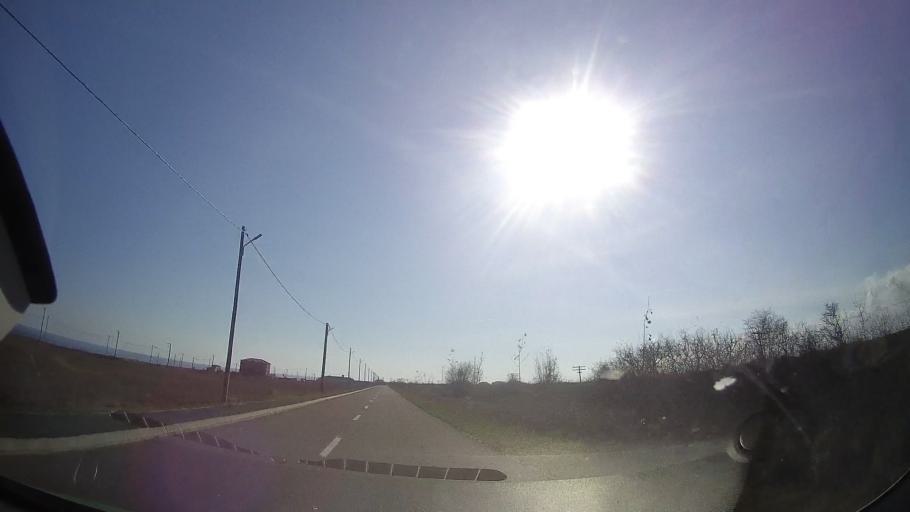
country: RO
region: Constanta
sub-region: Comuna Costinesti
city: Schitu
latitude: 43.9307
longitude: 28.6316
